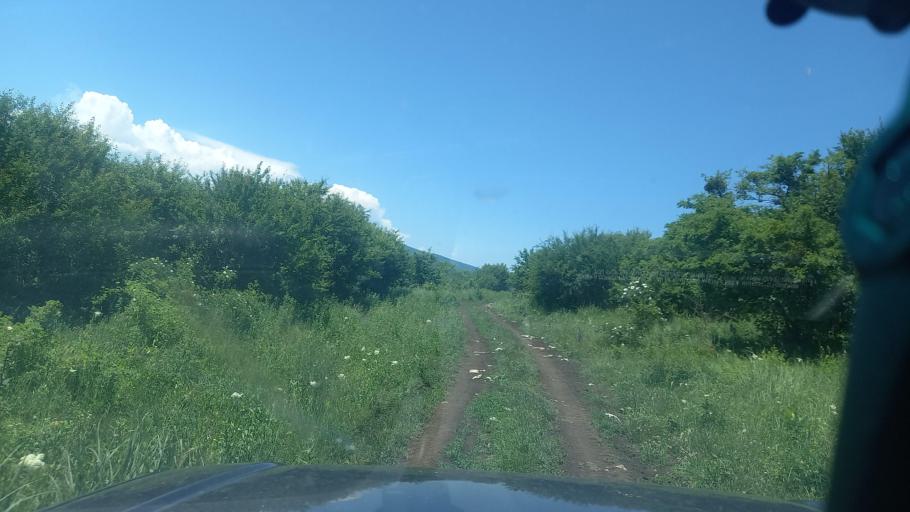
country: RU
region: Karachayevo-Cherkesiya
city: Pregradnaya
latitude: 44.1049
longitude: 41.1334
